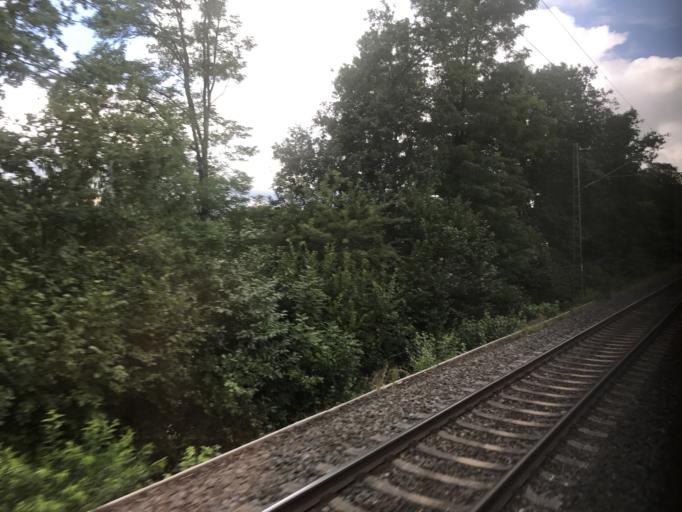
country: DE
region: Hesse
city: Schwalmstadt
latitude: 50.9155
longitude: 9.1946
